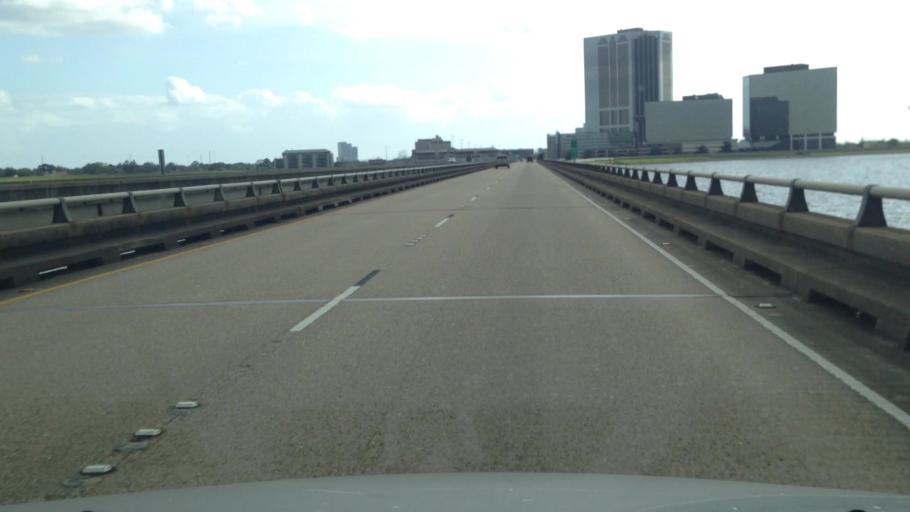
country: US
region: Louisiana
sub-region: Jefferson Parish
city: Metairie
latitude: 30.0266
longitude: -90.1533
